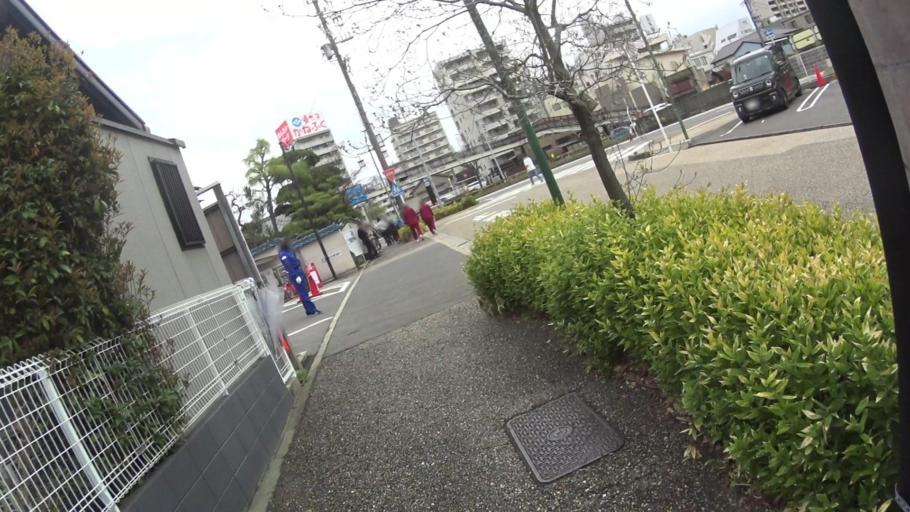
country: JP
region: Aichi
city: Nagoya-shi
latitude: 35.1199
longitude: 136.9069
